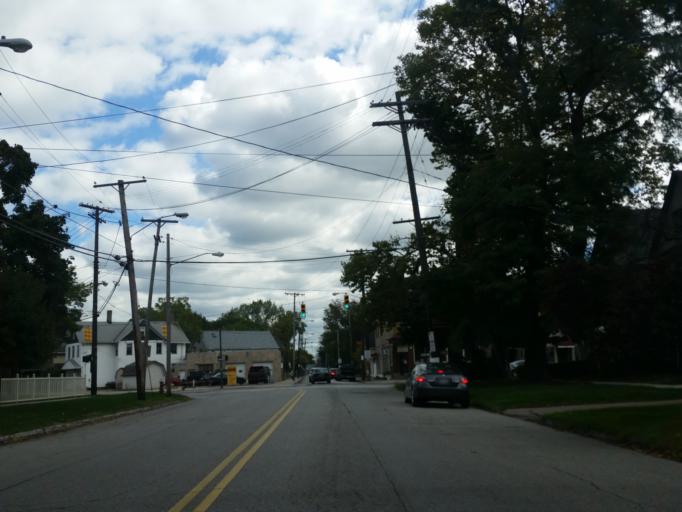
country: US
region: Ohio
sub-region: Cuyahoga County
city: Cleveland
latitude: 41.4774
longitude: -81.6882
